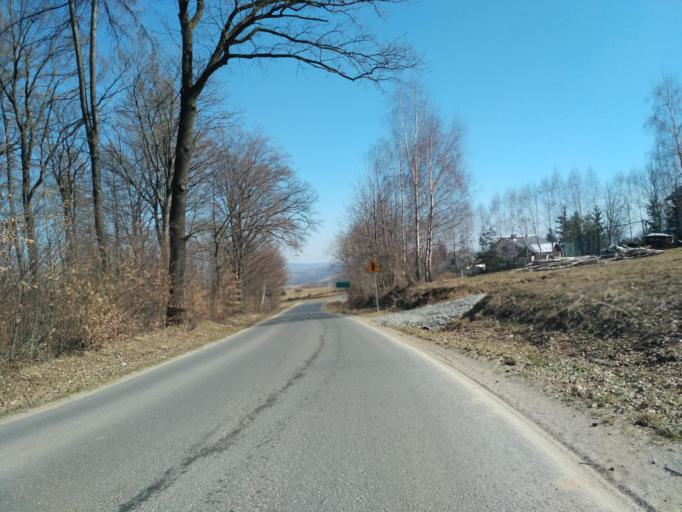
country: PL
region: Subcarpathian Voivodeship
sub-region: Powiat ropczycko-sedziszowski
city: Niedzwiada
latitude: 49.9663
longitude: 21.4661
